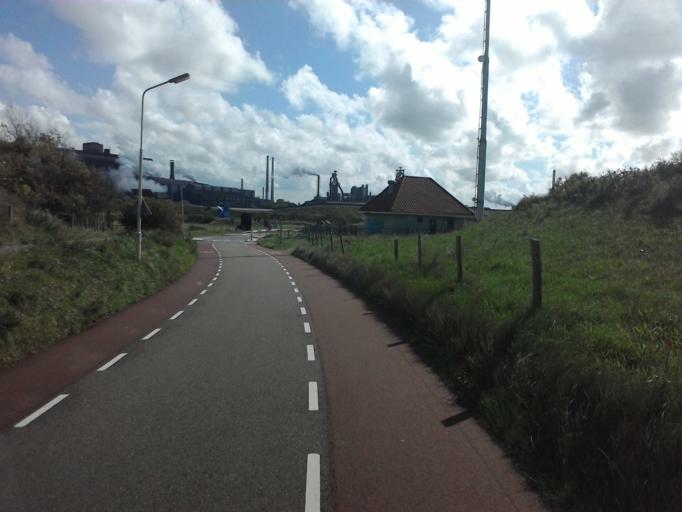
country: NL
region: North Holland
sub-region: Gemeente Velsen
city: Velsen-Zuid
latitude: 52.4897
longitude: 4.5911
